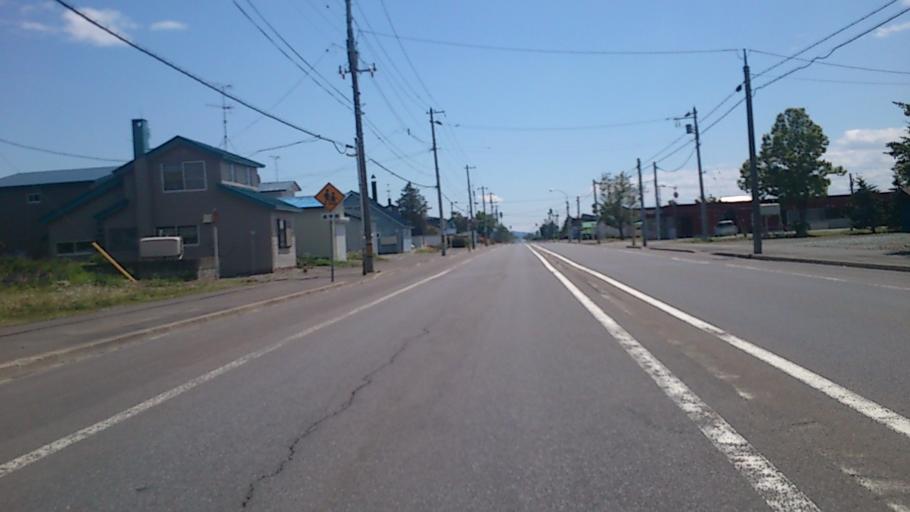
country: JP
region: Hokkaido
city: Nayoro
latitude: 44.2391
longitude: 142.3950
